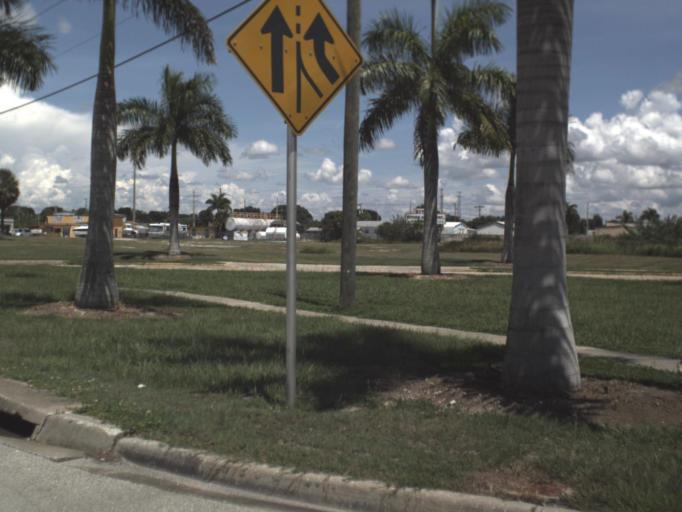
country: US
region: Florida
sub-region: Charlotte County
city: Punta Gorda
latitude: 26.9309
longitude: -82.0473
